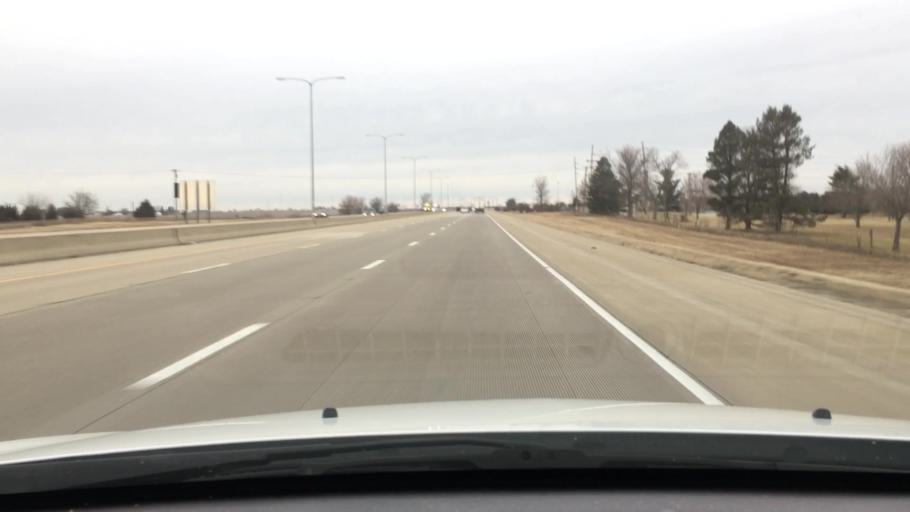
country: US
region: Illinois
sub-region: McLean County
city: Normal
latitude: 40.5153
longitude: -89.0285
